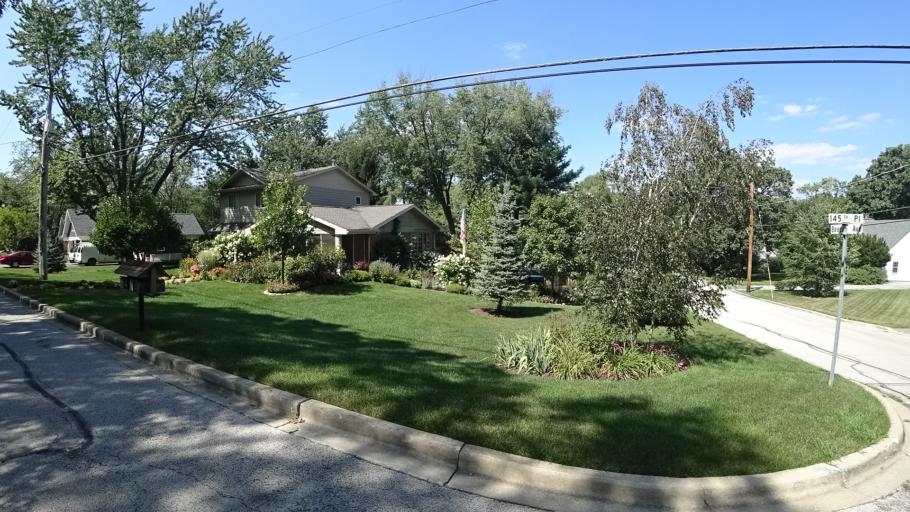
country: US
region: Illinois
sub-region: Cook County
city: Orland Park
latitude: 41.6258
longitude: -87.8591
